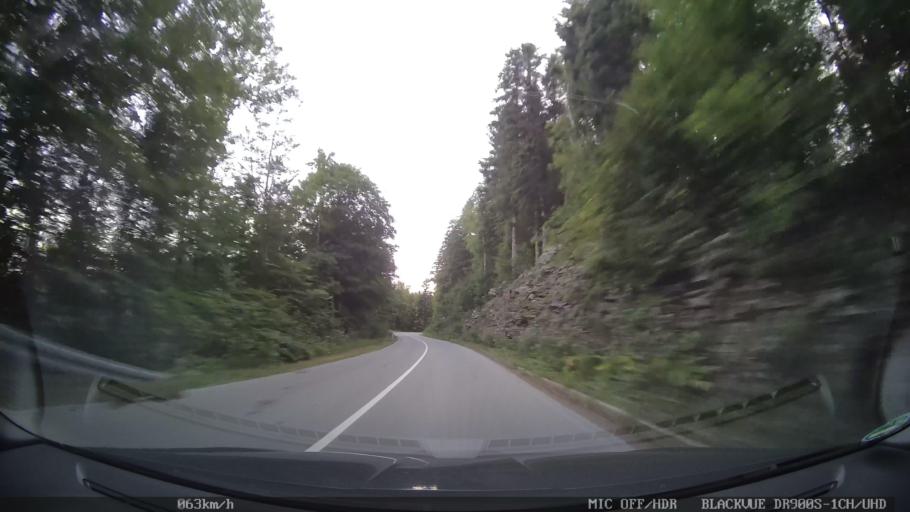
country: HR
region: Primorsko-Goranska
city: Novi Vinodolski
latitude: 45.1749
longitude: 14.9743
